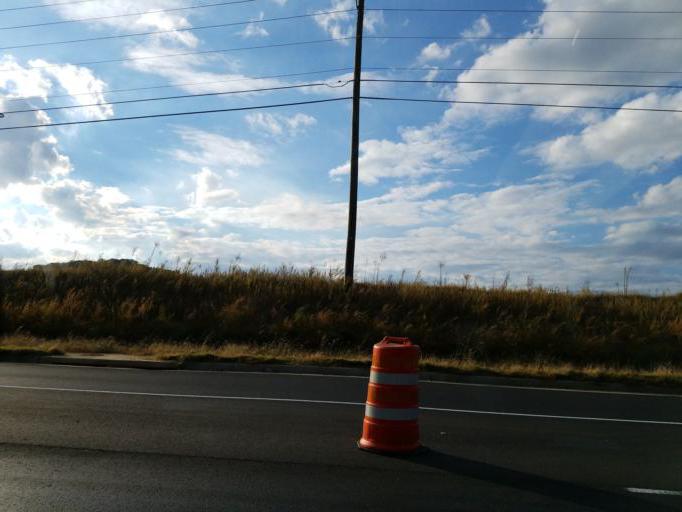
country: US
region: Georgia
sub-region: Bartow County
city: Cartersville
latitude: 34.2090
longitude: -84.7985
